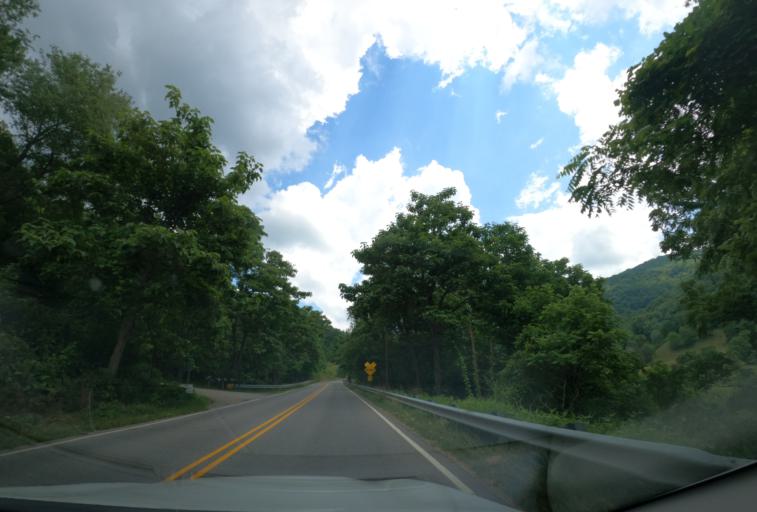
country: US
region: North Carolina
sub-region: Haywood County
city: Waynesville
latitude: 35.4743
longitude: -82.9487
